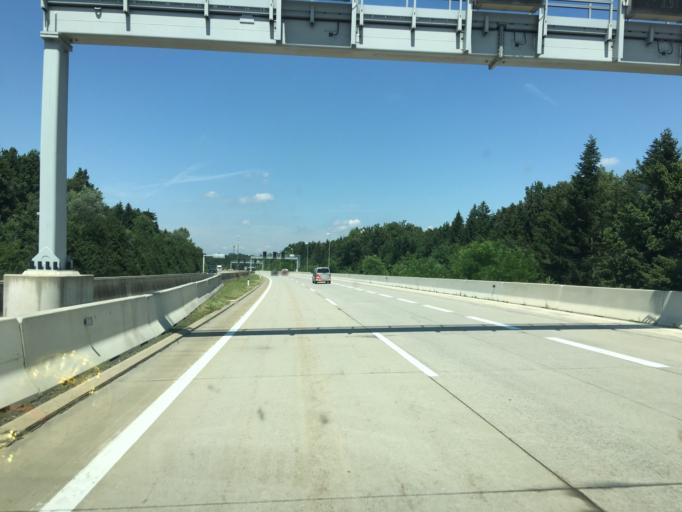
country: AT
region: Styria
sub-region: Politischer Bezirk Leibnitz
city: Strass in Steiermark
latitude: 46.7260
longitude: 15.6467
